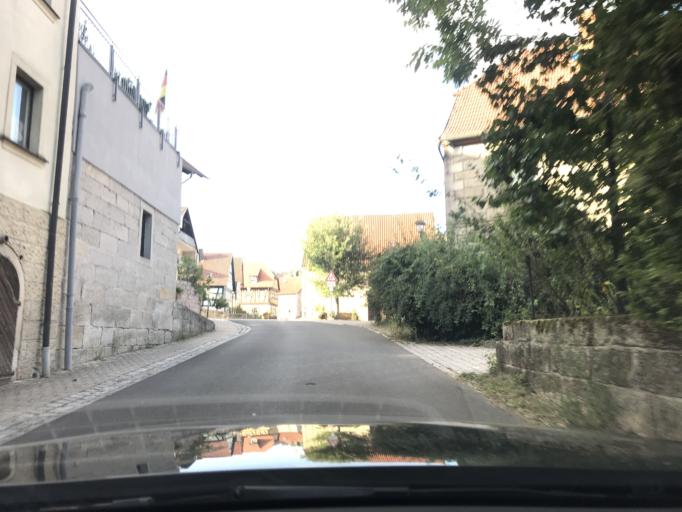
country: DE
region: Bavaria
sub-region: Regierungsbezirk Unterfranken
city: Breitbrunn
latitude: 50.0349
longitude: 10.6897
